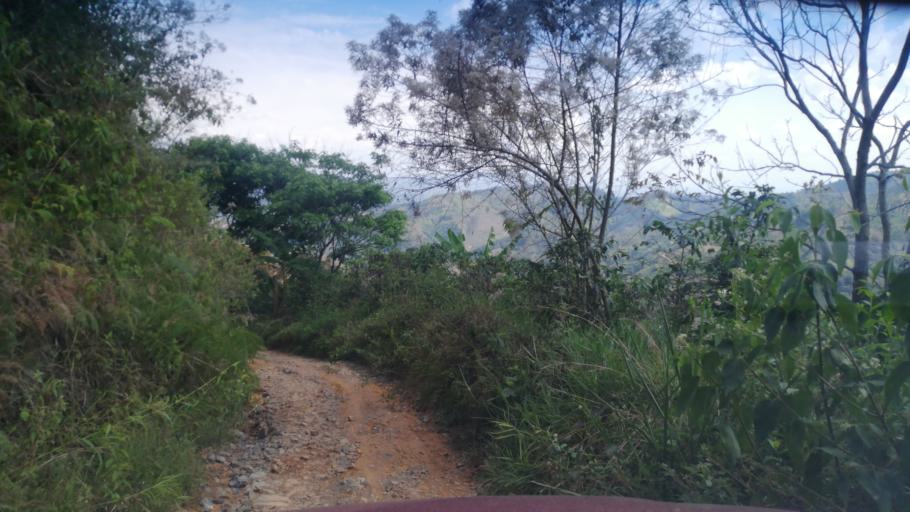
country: CO
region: Risaralda
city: Balboa
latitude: 4.9245
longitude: -75.9574
